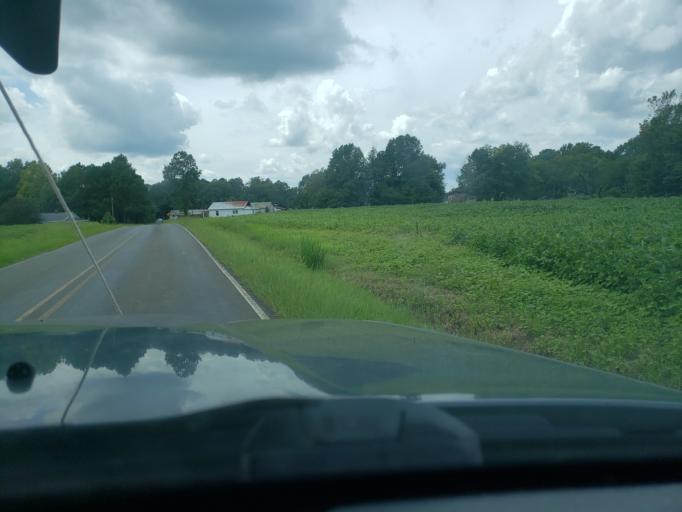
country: US
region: North Carolina
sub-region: Wake County
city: Zebulon
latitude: 35.8855
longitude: -78.3492
